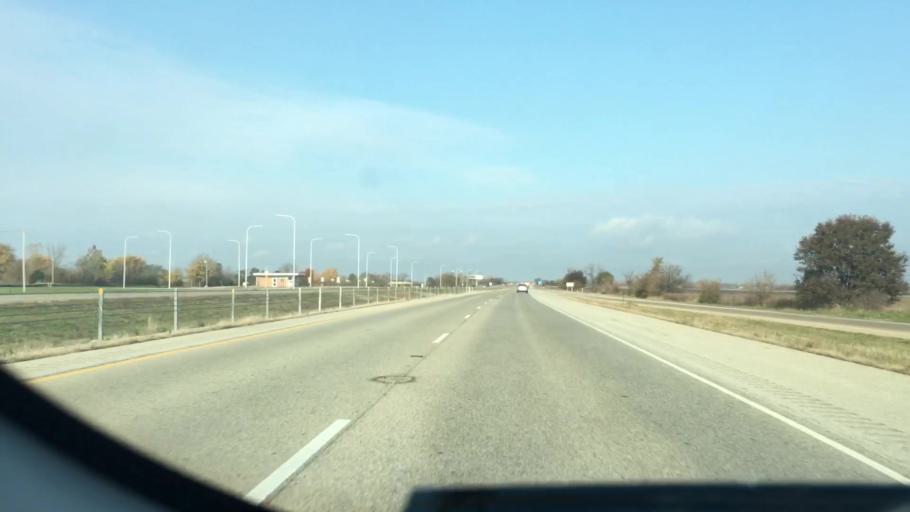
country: US
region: Illinois
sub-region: McLean County
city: Twin Grove
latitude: 40.5566
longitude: -89.1050
